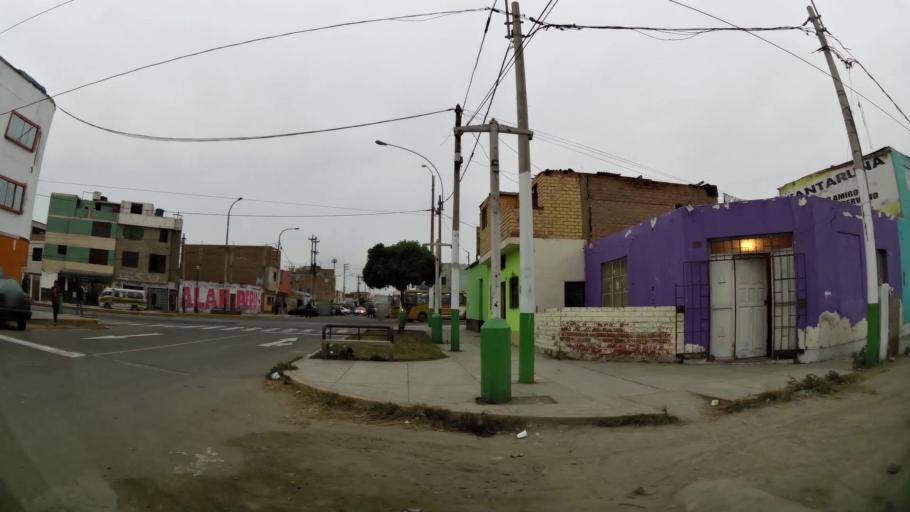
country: PE
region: Callao
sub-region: Callao
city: Callao
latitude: -12.0678
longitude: -77.1310
